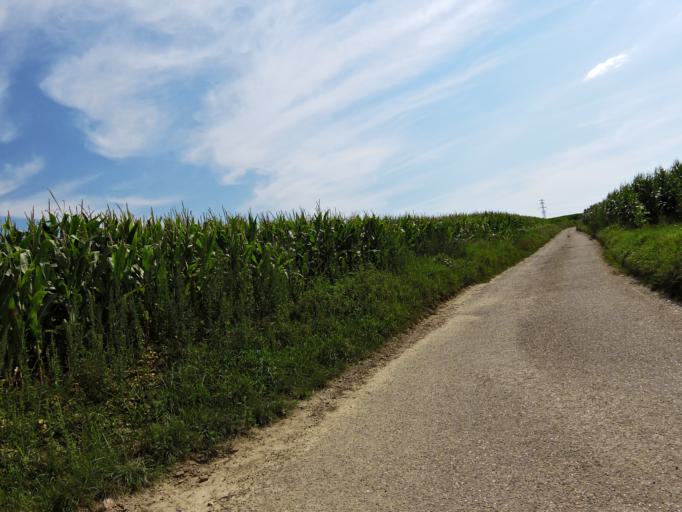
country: NL
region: Limburg
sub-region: Gemeente Voerendaal
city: Kunrade
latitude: 50.8616
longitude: 5.9079
